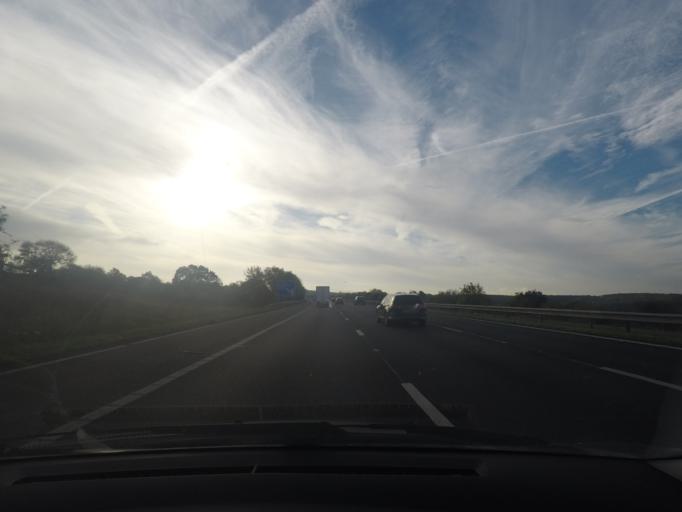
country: GB
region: England
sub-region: Barnsley
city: Darton
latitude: 53.5661
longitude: -1.5397
